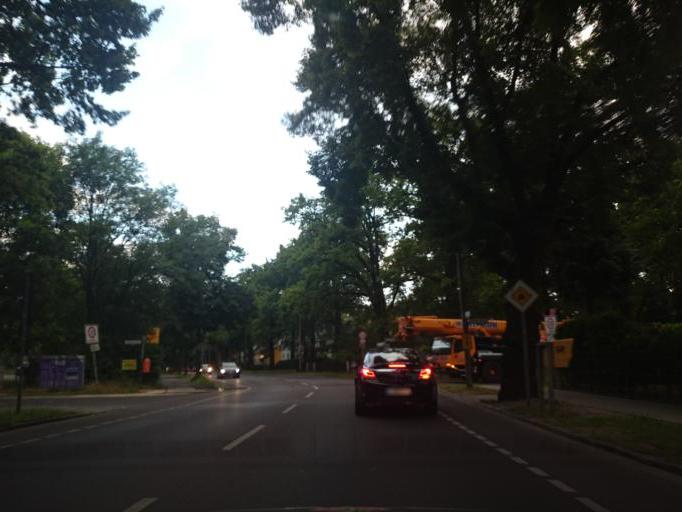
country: DE
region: Berlin
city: Biesdorf
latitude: 52.4929
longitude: 13.5611
